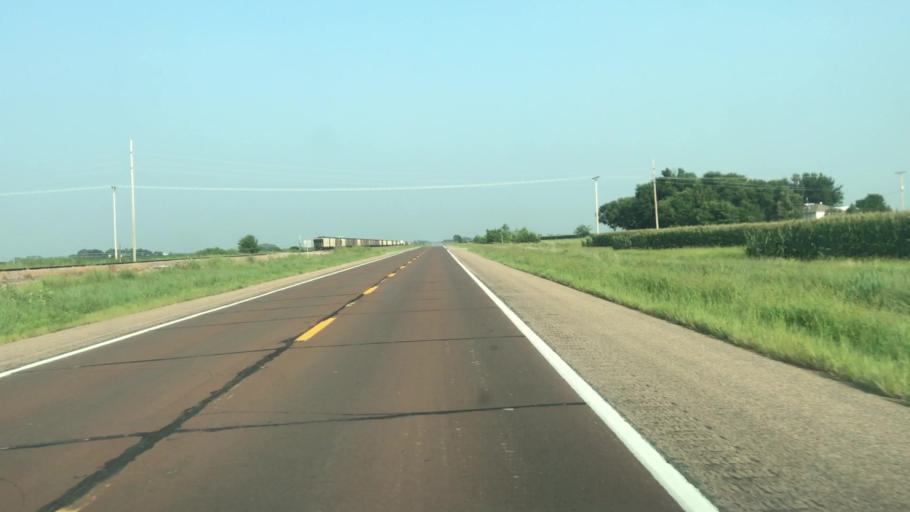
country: US
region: Nebraska
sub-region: Hall County
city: Wood River
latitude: 40.9984
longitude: -98.5906
